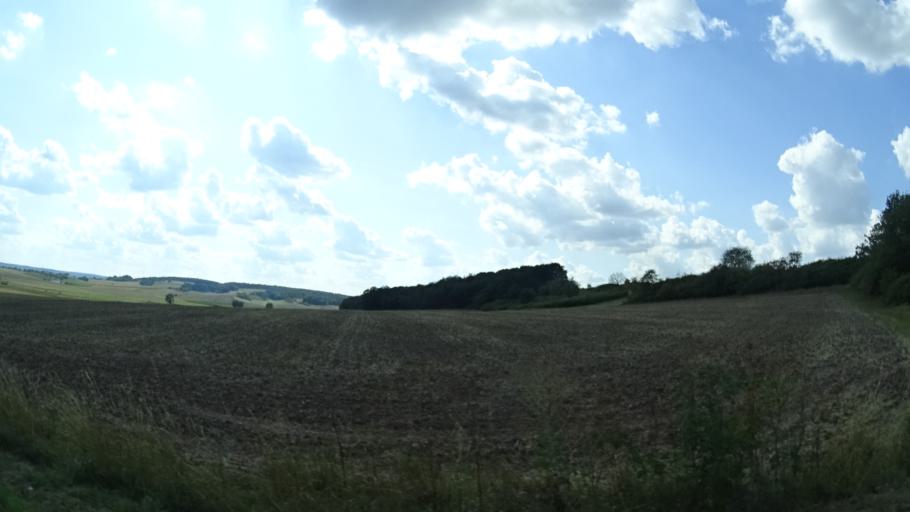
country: DE
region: Bavaria
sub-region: Regierungsbezirk Unterfranken
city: Trappstadt
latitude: 50.3082
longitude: 10.5696
